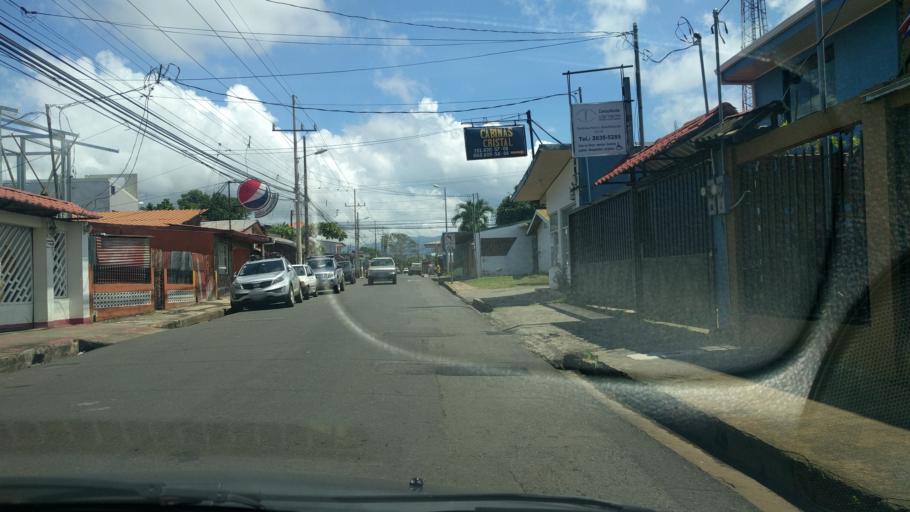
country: CR
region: Puntarenas
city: Esparza
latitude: 9.9919
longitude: -84.6645
